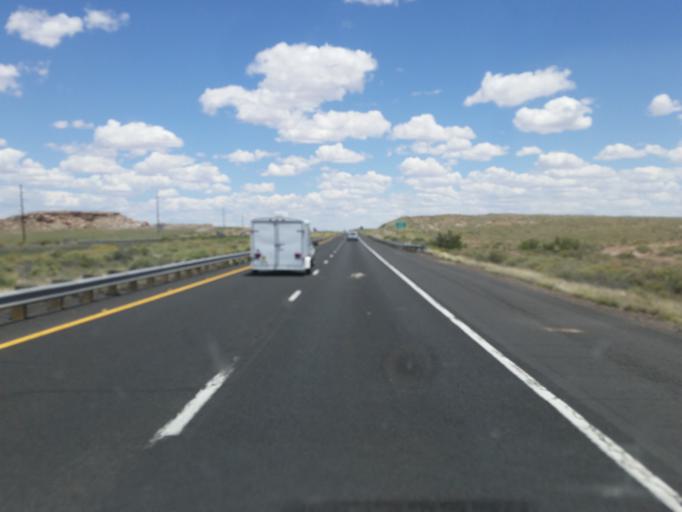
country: US
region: Arizona
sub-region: Navajo County
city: Holbrook
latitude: 34.9910
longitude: -109.9848
